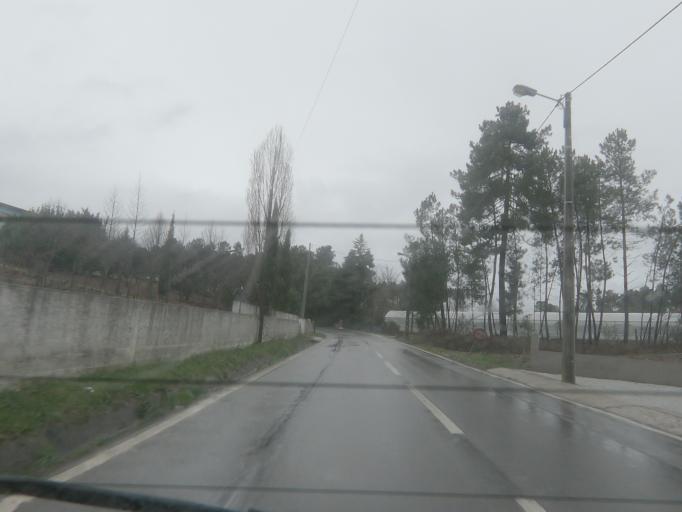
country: PT
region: Vila Real
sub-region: Vila Real
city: Vila Real
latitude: 41.2650
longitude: -7.6948
